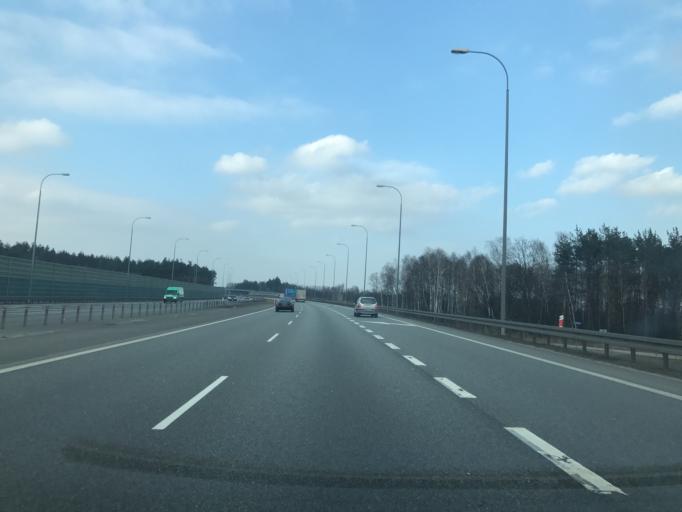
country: PL
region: Kujawsko-Pomorskie
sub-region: Powiat torunski
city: Lubicz Dolny
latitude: 53.0148
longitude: 18.7360
